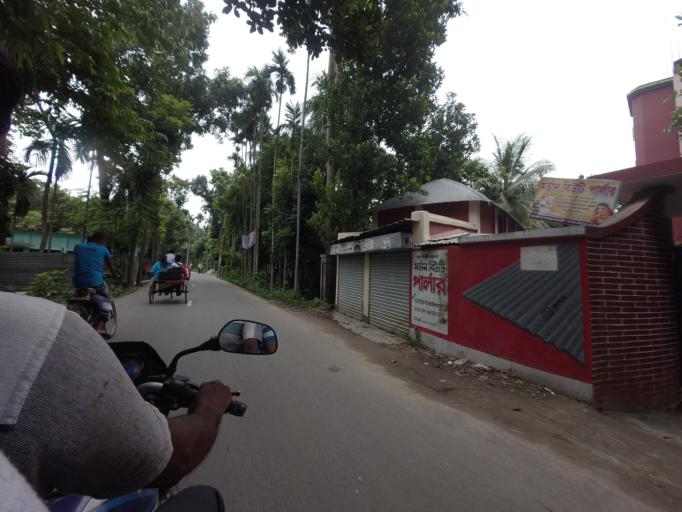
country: BD
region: Khulna
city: Kalia
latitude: 23.1779
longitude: 89.6476
